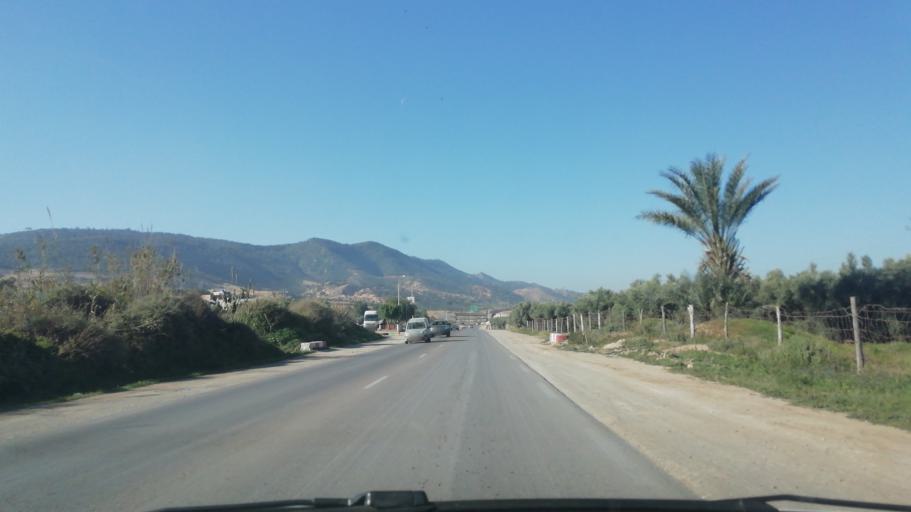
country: DZ
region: Mascara
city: Sig
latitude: 35.5328
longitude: -0.1446
